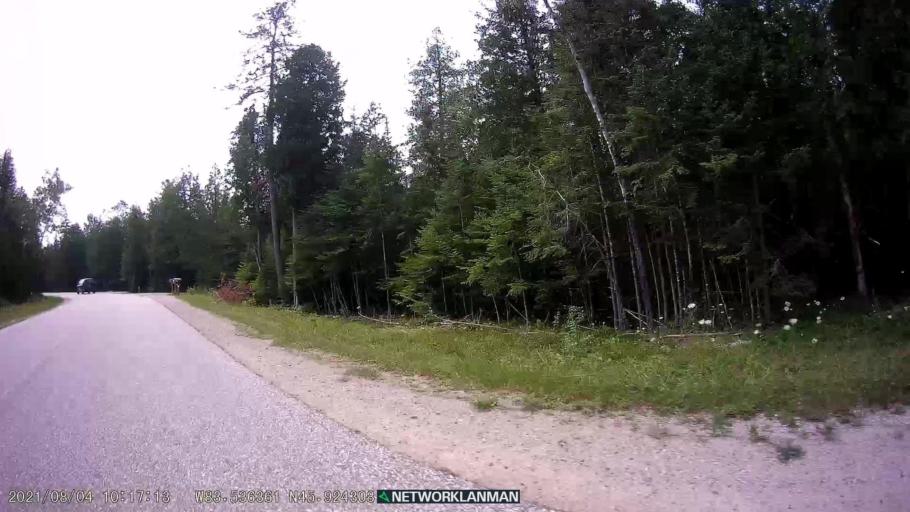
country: CA
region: Ontario
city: Thessalon
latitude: 45.9243
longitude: -83.5365
